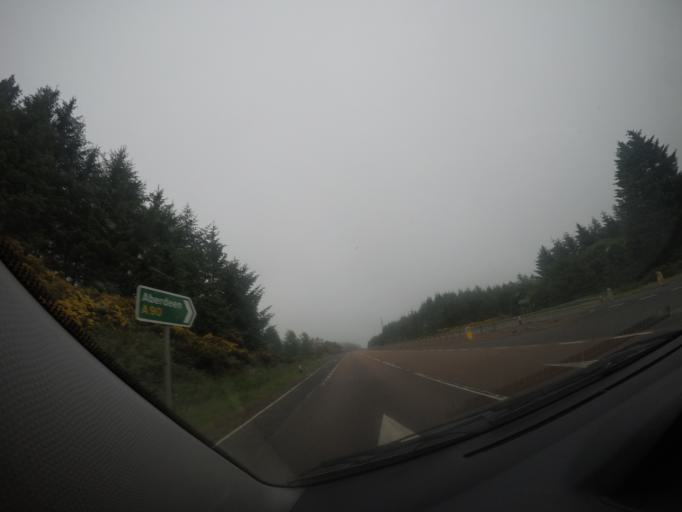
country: GB
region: Scotland
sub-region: Dundee City
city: Dundee
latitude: 56.5467
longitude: -2.9409
